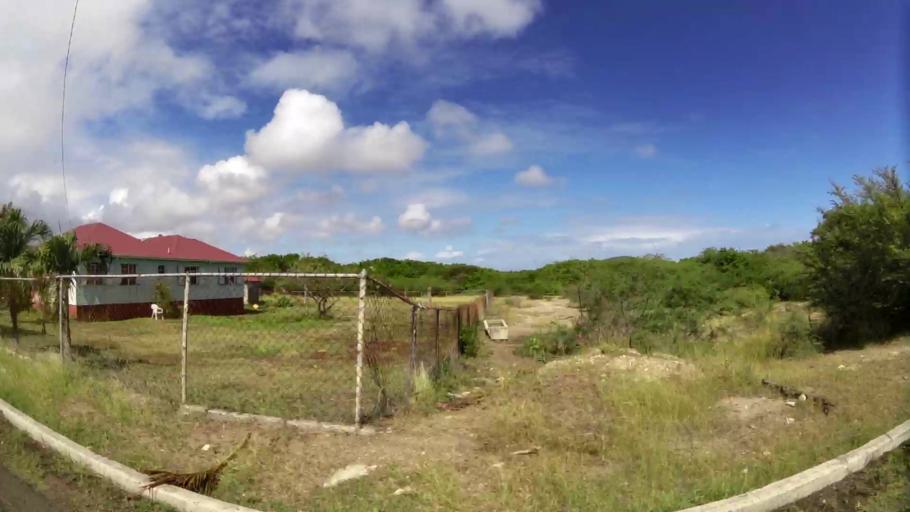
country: AG
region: Saint Paul
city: Falmouth
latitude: 17.0344
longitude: -61.7486
